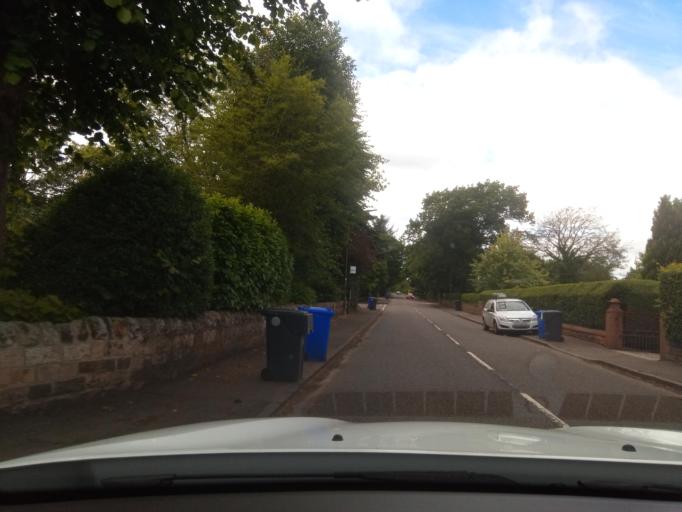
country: GB
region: Scotland
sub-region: Stirling
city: Dunblane
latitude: 56.1910
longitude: -3.9767
